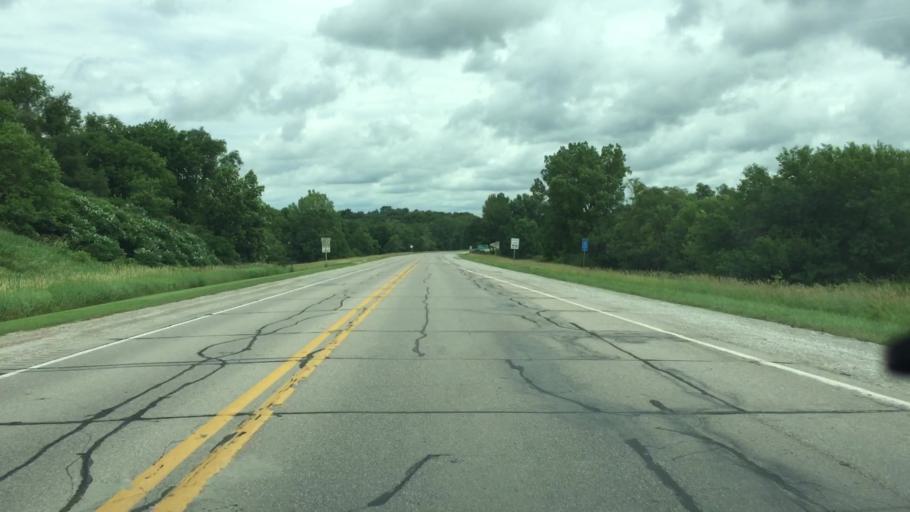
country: US
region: Iowa
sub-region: Jasper County
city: Monroe
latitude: 41.5292
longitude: -93.1019
